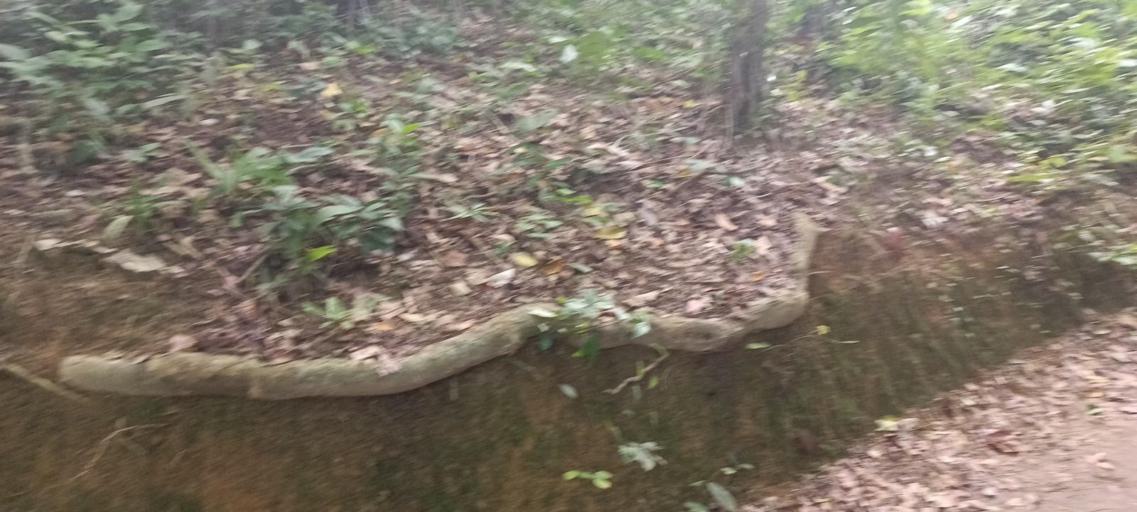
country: MY
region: Penang
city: Kampung Sungai Ara
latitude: 5.2714
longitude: 100.2686
